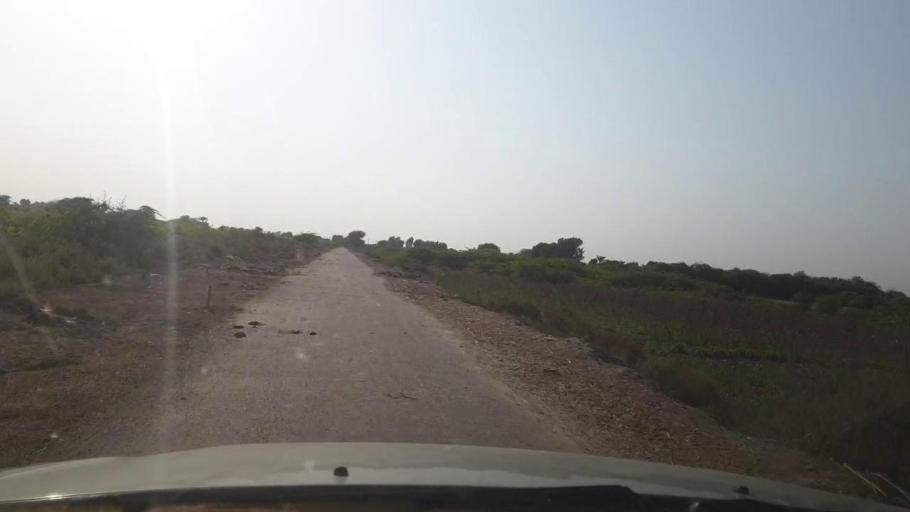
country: PK
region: Sindh
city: Tando Ghulam Ali
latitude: 25.1892
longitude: 68.9468
